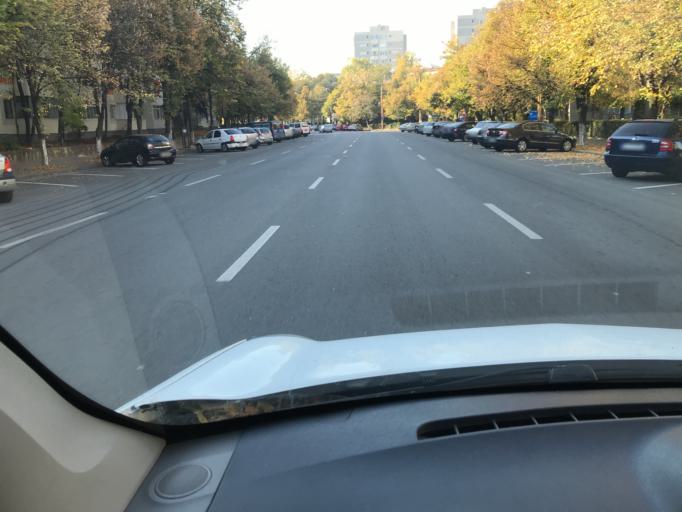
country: RO
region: Olt
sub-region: Municipiul Slatina
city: Slatina
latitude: 44.4346
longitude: 24.3696
